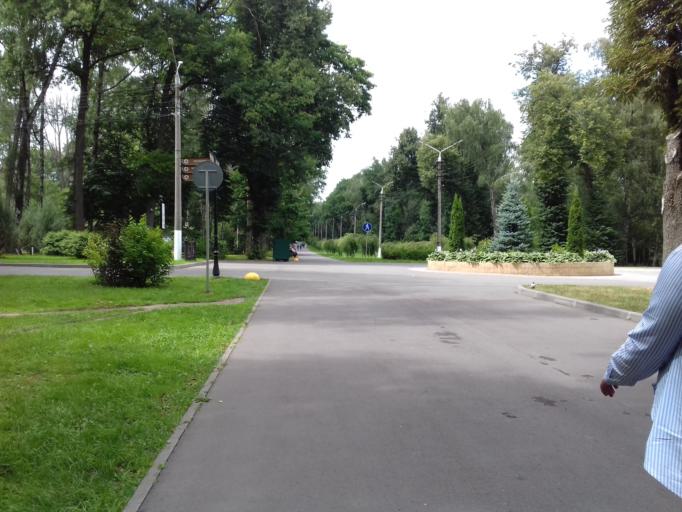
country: RU
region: Tula
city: Tula
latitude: 54.1844
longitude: 37.5938
